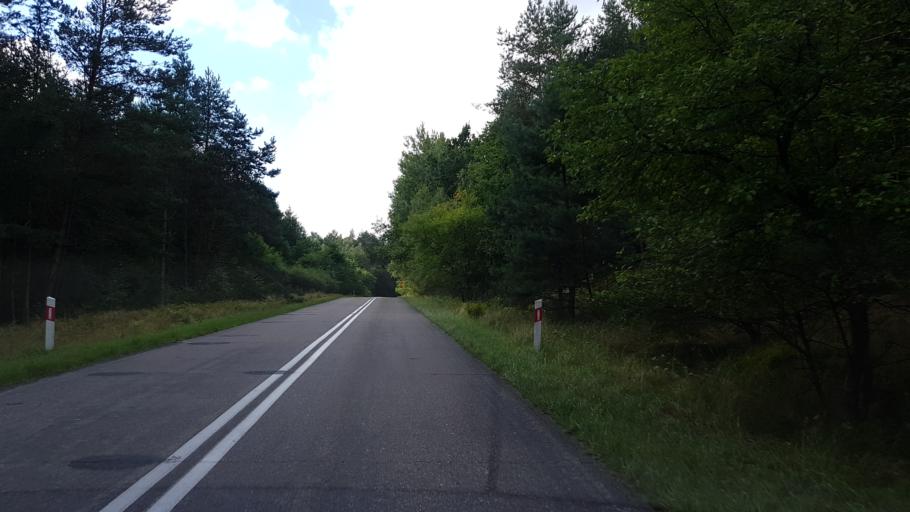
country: PL
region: West Pomeranian Voivodeship
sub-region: Powiat bialogardzki
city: Tychowo
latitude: 54.0523
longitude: 16.3012
